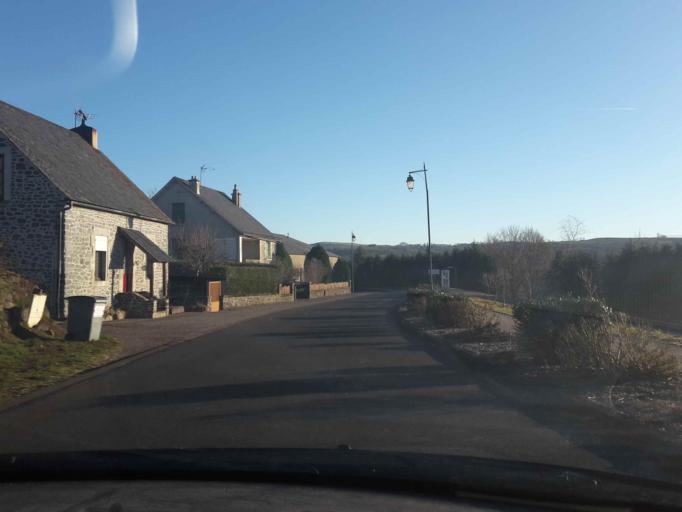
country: FR
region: Auvergne
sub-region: Departement du Cantal
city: Ydes
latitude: 45.2489
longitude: 2.5371
